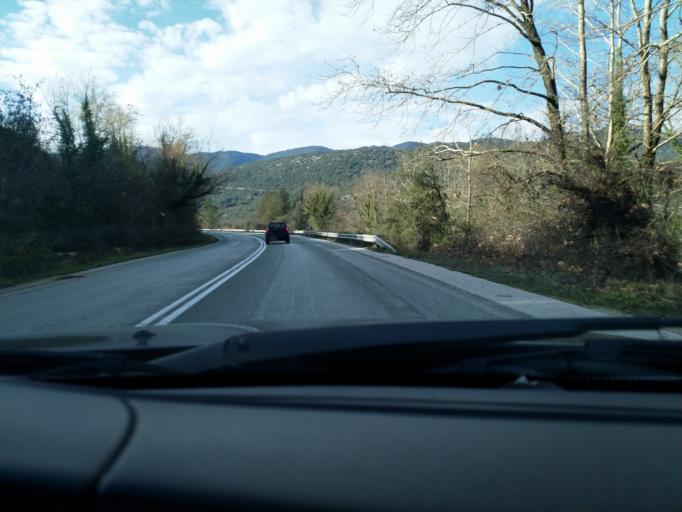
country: GR
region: Epirus
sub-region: Nomos Ioanninon
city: Agia Kyriaki
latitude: 39.4518
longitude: 20.8699
